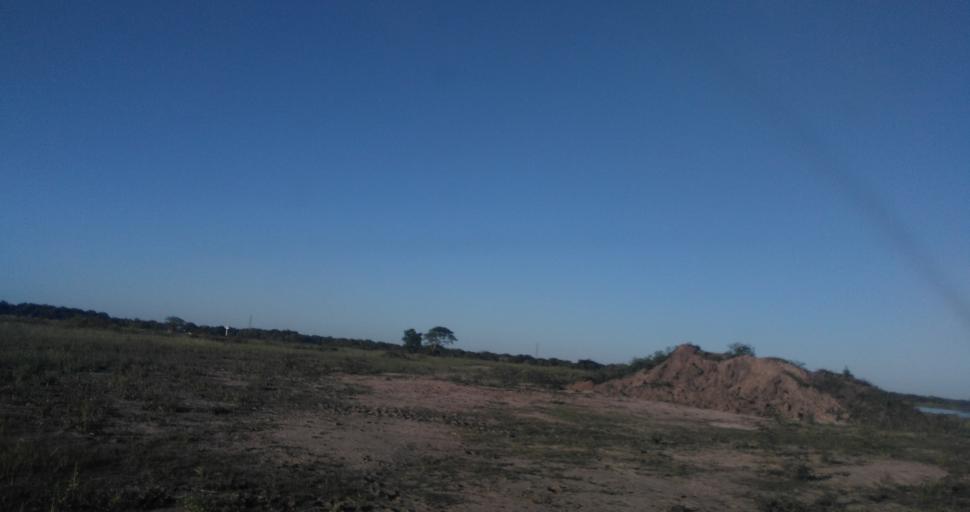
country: AR
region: Chaco
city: Fontana
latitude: -27.3956
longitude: -58.9837
